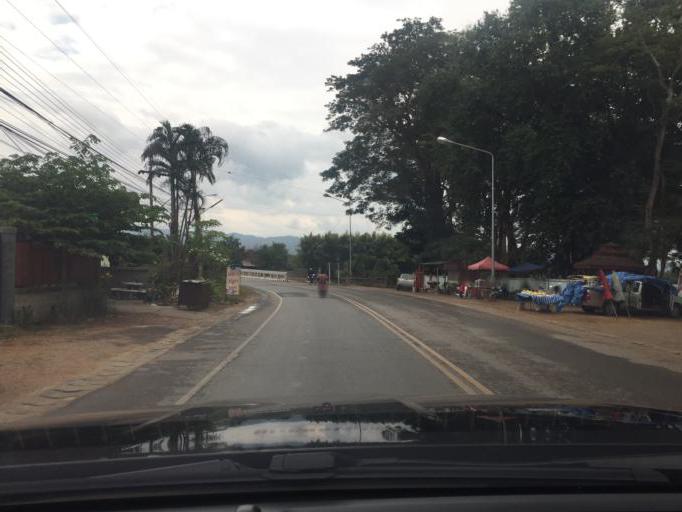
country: TH
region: Phayao
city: Pong
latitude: 19.1687
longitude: 100.2841
